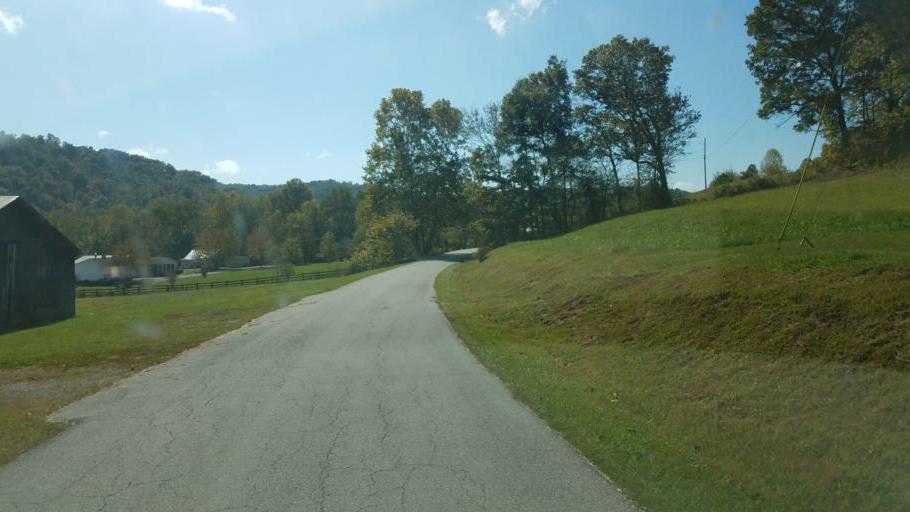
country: US
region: Kentucky
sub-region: Fleming County
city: Flemingsburg
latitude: 38.4457
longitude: -83.5519
